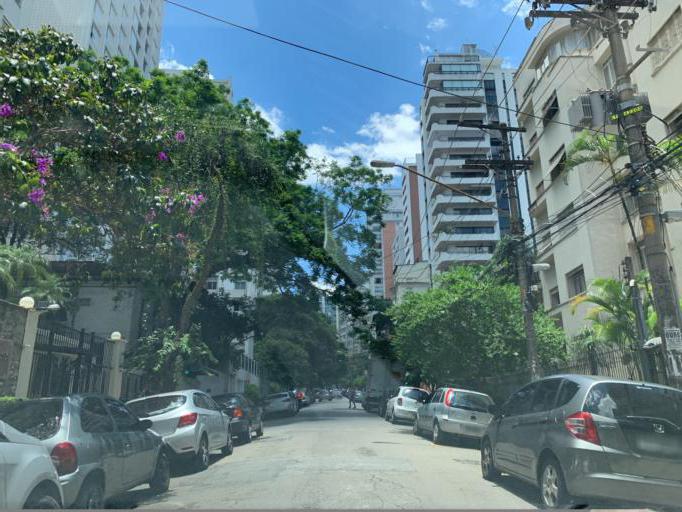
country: BR
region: Sao Paulo
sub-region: Sao Paulo
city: Sao Paulo
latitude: -23.5356
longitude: -46.6605
